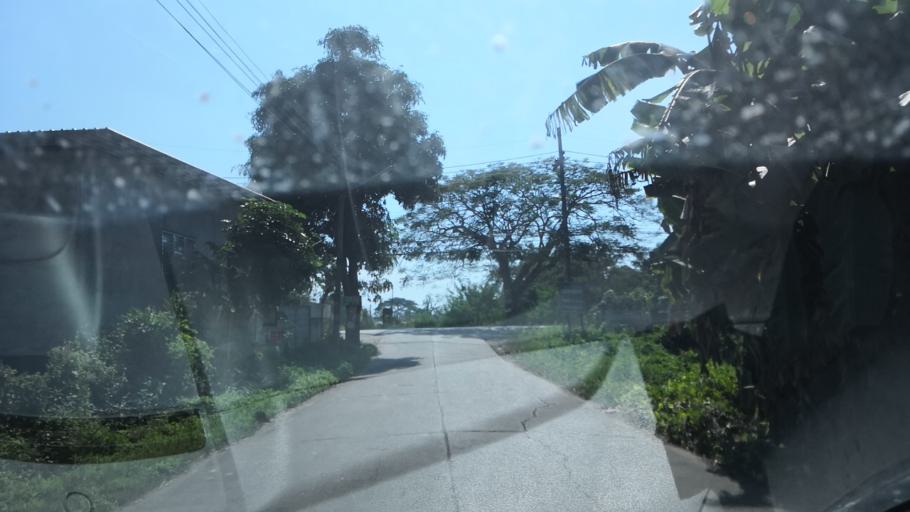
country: TH
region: Chiang Rai
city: Wiang Chai
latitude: 19.8800
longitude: 99.9417
